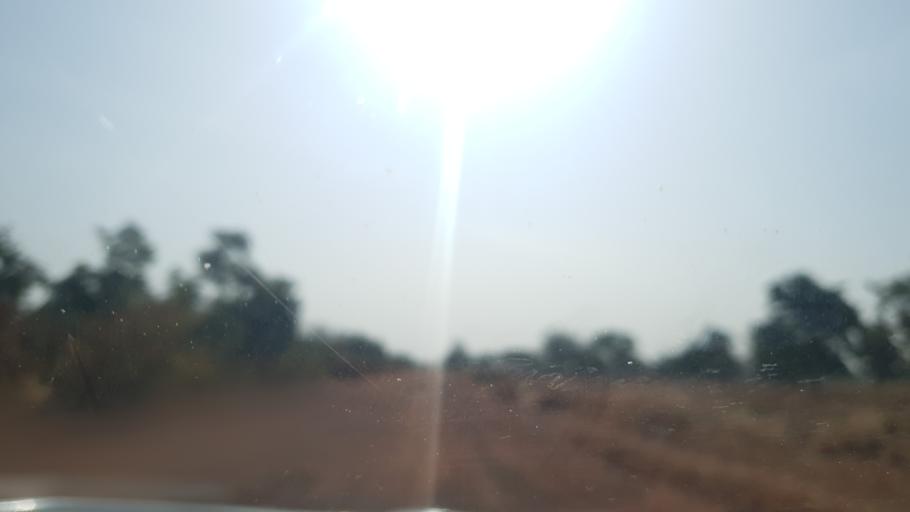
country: ML
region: Koulikoro
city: Dioila
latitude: 12.7017
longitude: -6.7642
